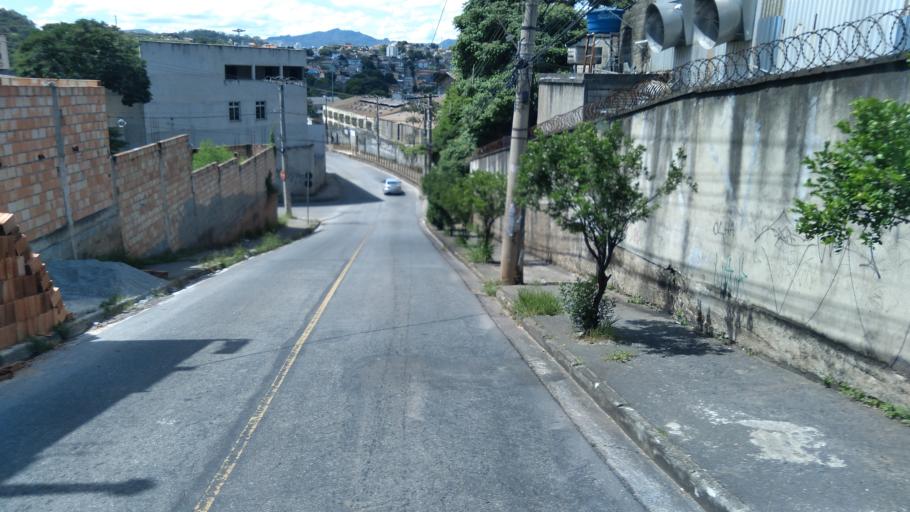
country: BR
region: Minas Gerais
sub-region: Belo Horizonte
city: Belo Horizonte
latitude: -19.8545
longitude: -43.8972
